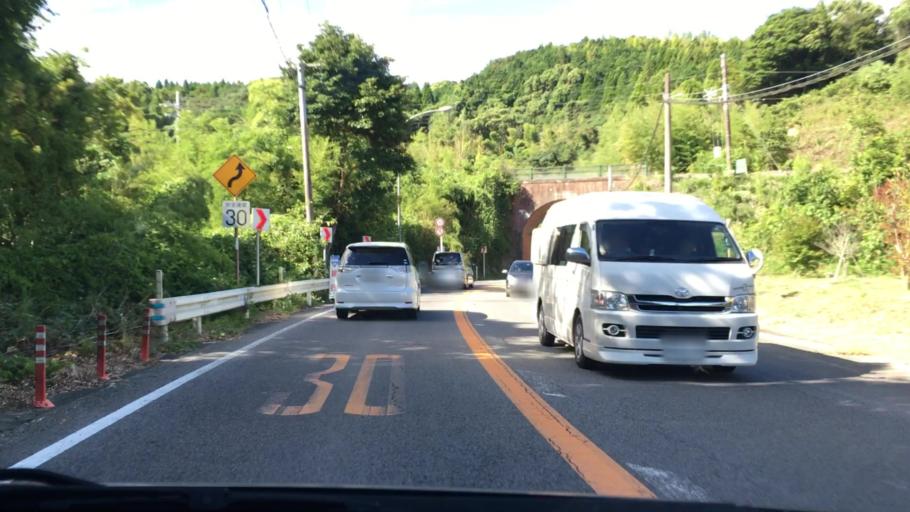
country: JP
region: Saga Prefecture
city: Takeocho-takeo
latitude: 33.1881
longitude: 129.9866
